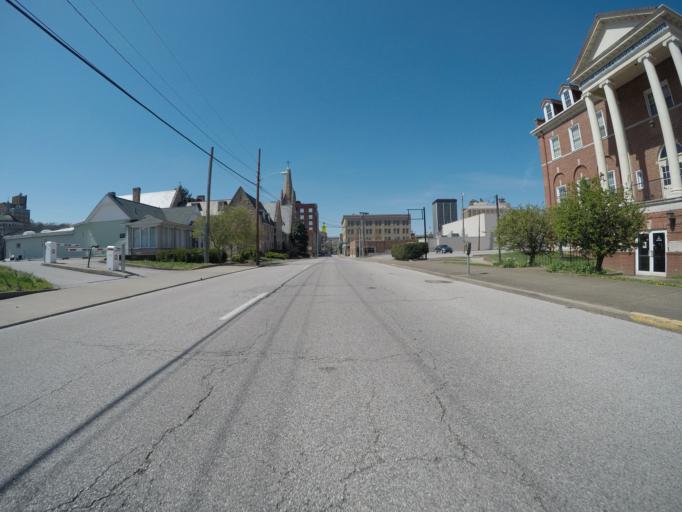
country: US
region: West Virginia
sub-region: Kanawha County
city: Charleston
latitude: 38.3469
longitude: -81.6311
